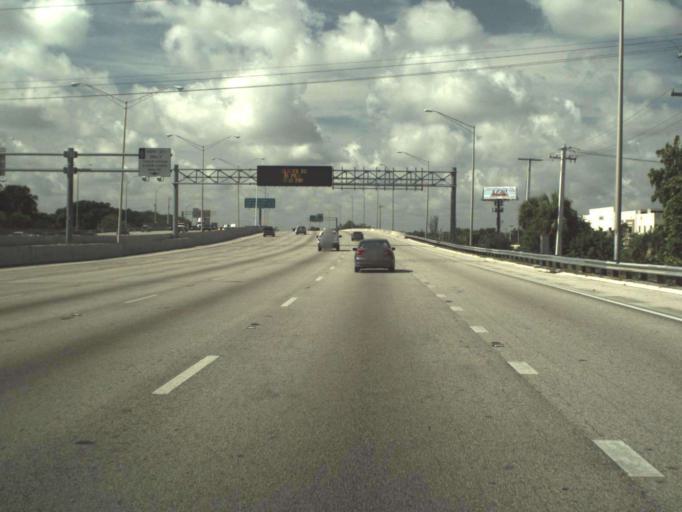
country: US
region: Florida
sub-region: Palm Beach County
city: Lake Clarke Shores
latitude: 26.6696
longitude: -80.0709
